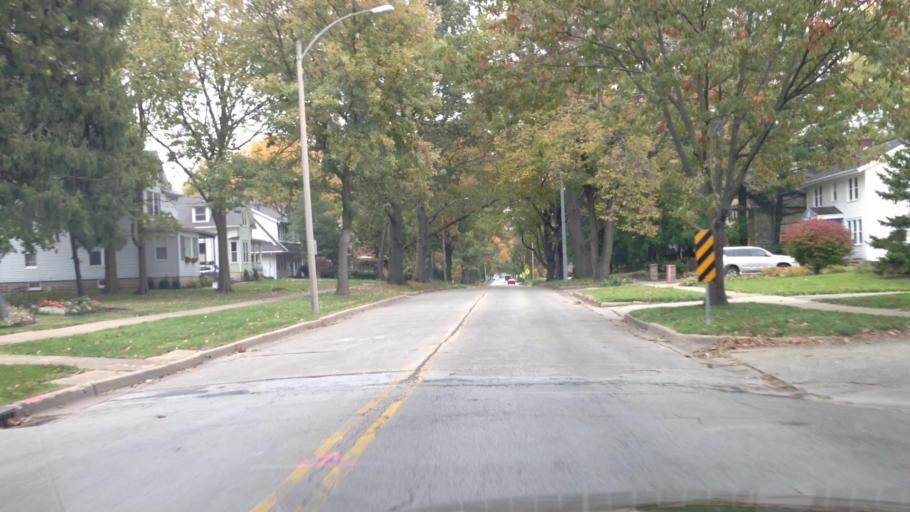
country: US
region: Illinois
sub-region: Champaign County
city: Champaign
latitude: 40.1101
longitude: -88.2575
